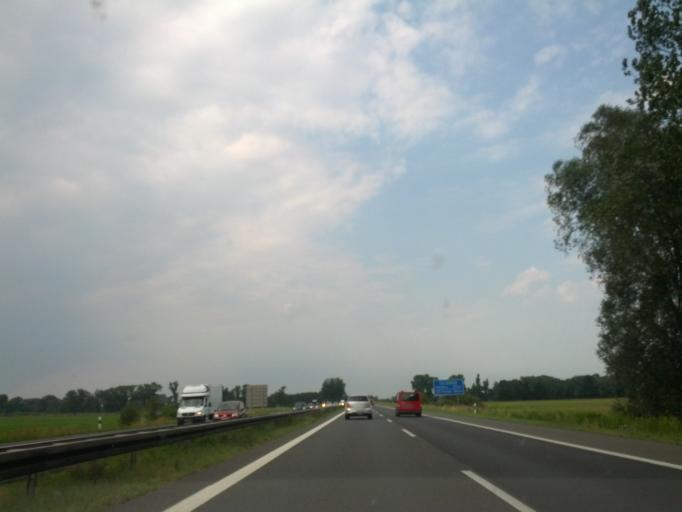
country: DE
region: Brandenburg
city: Fehrbellin
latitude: 52.8121
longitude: 12.7943
